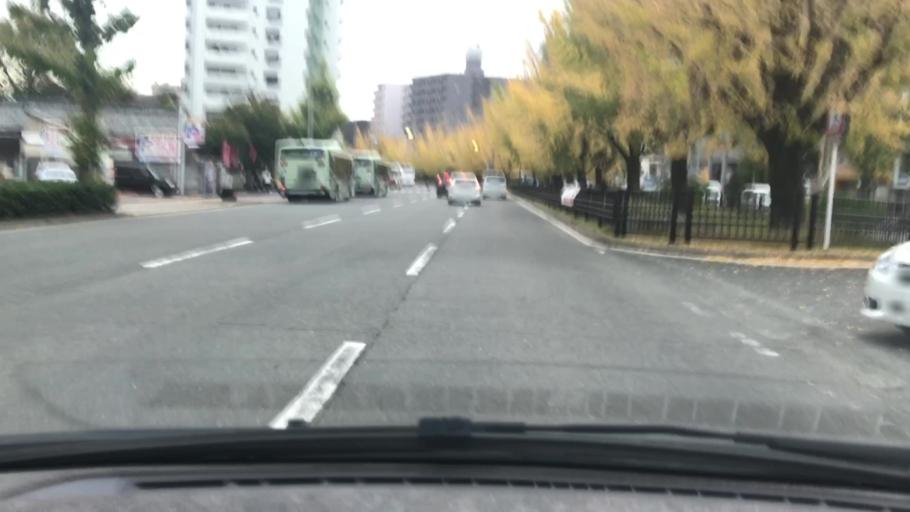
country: JP
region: Kyoto
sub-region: Kyoto-shi
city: Kamigyo-ku
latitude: 35.0368
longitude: 135.7517
